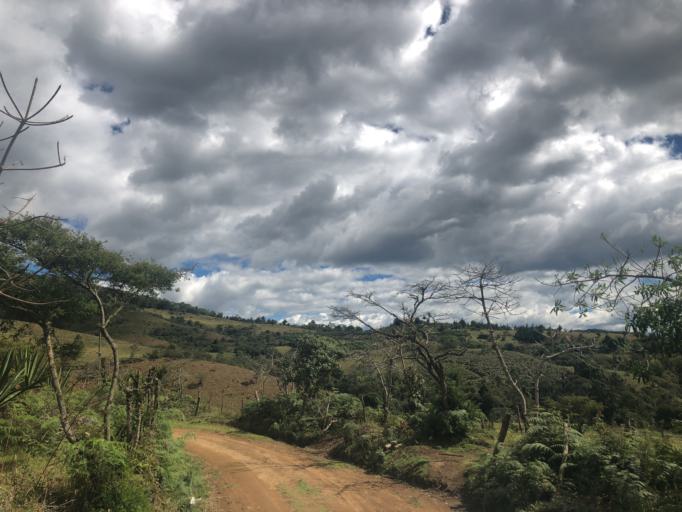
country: CO
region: Cauca
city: Silvia
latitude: 2.6833
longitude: -76.4386
